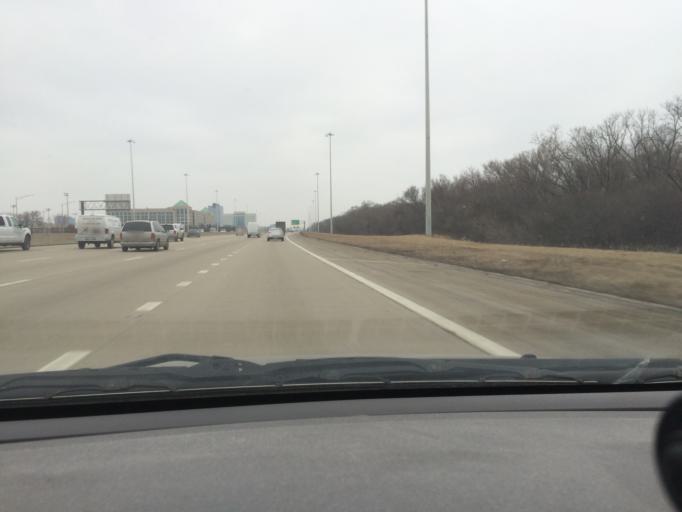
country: US
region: Illinois
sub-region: DuPage County
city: Itasca
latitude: 42.0194
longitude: -88.0308
